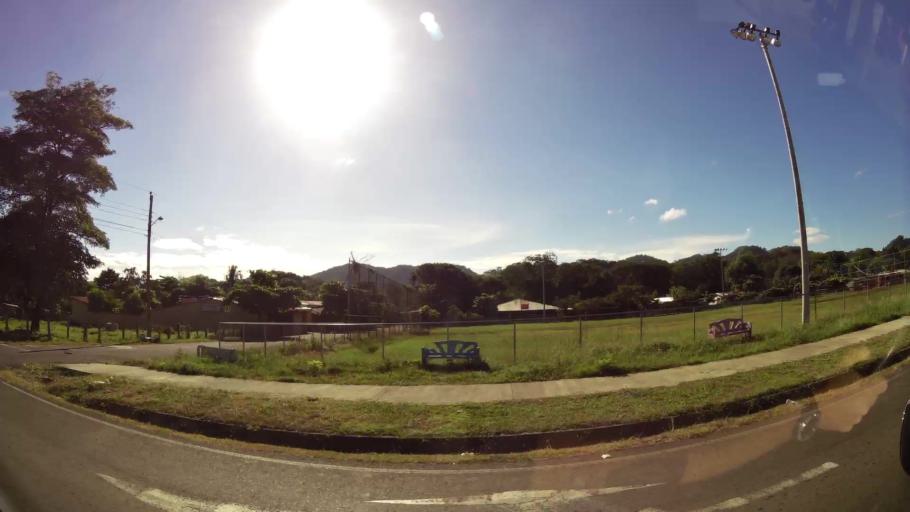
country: CR
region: Guanacaste
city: Belen
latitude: 10.3901
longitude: -85.6191
